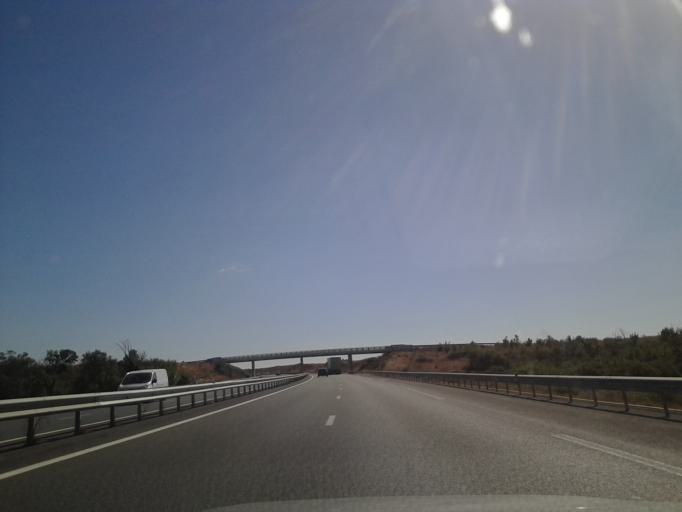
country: FR
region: Languedoc-Roussillon
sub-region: Departement de l'Herault
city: Valros
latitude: 43.4111
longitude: 3.3700
